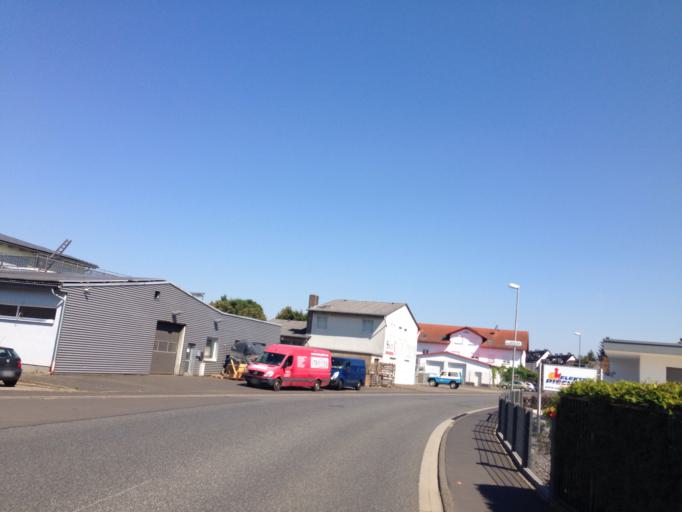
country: DE
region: Hesse
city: Lollar
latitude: 50.6440
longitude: 8.7012
